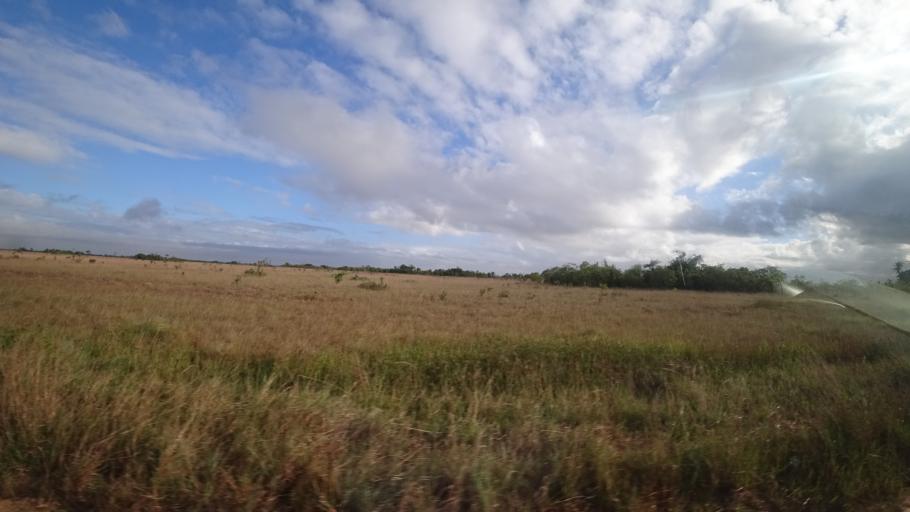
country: MZ
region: Sofala
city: Beira
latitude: -19.6821
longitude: 35.0549
